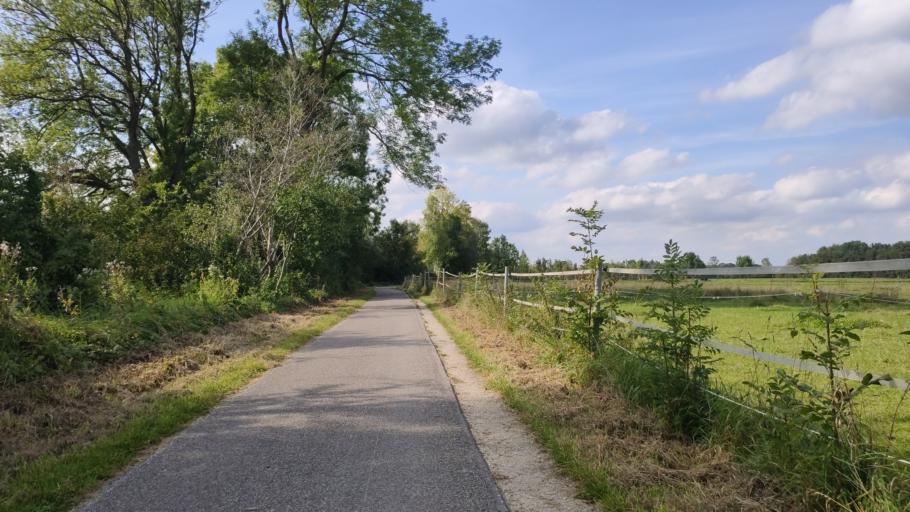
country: DE
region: Bavaria
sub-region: Upper Bavaria
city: Kaufering
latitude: 48.0956
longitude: 10.8691
